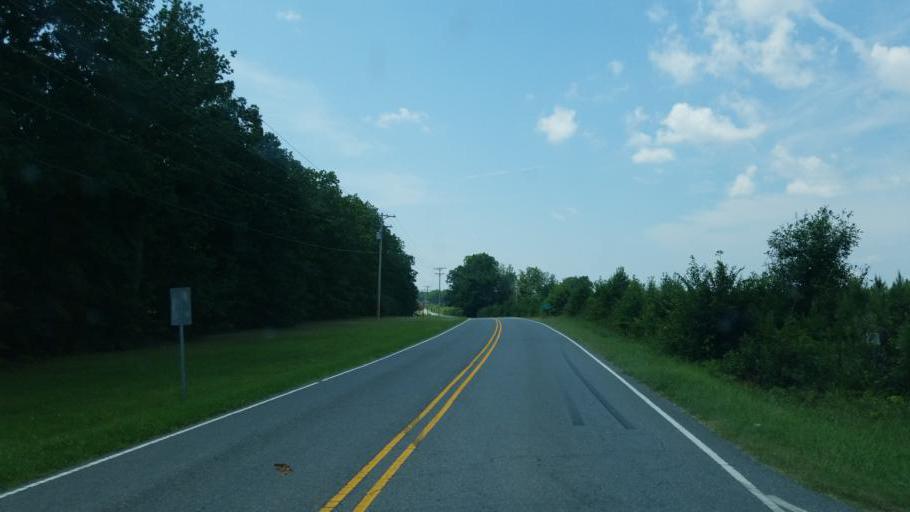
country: US
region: North Carolina
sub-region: Gaston County
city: Tryon
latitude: 35.3312
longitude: -81.3559
